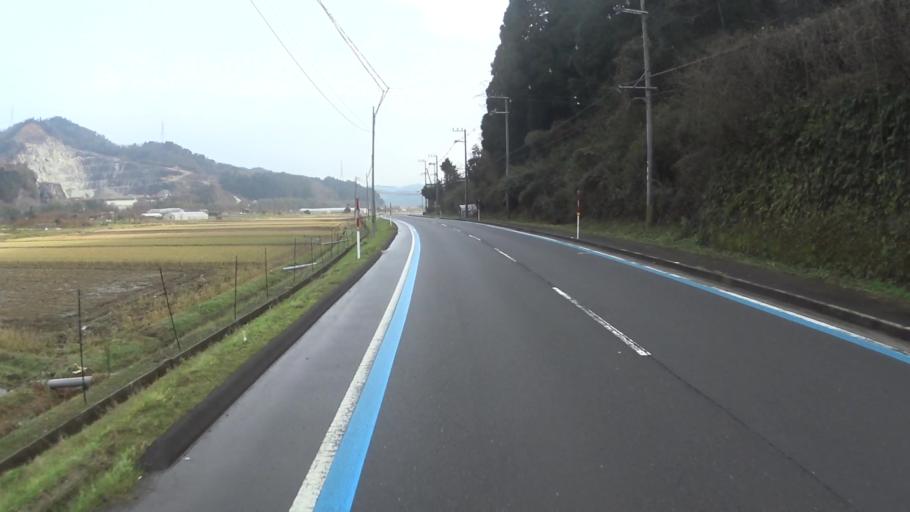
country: JP
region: Kyoto
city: Maizuru
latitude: 35.4260
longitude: 135.2287
